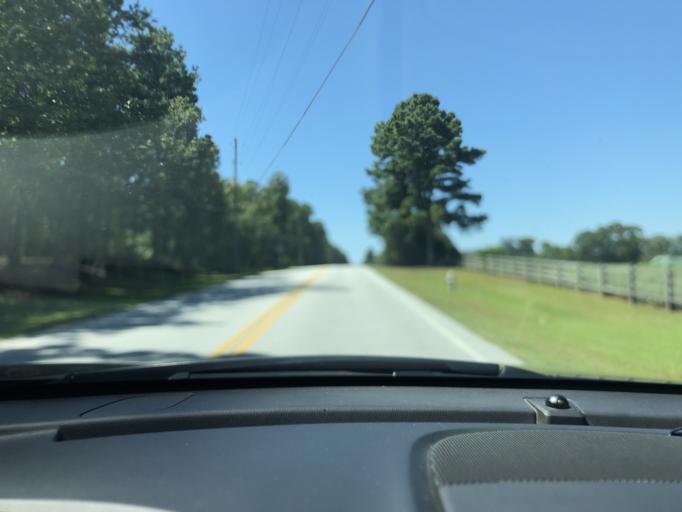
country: US
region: Georgia
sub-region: Walton County
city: Loganville
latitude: 33.9045
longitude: -83.8902
